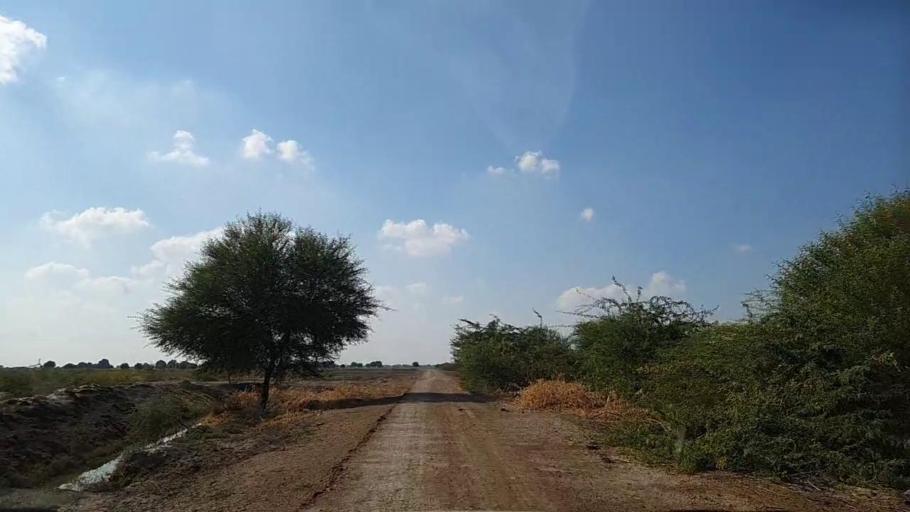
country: PK
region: Sindh
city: Pithoro
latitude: 25.6161
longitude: 69.3794
